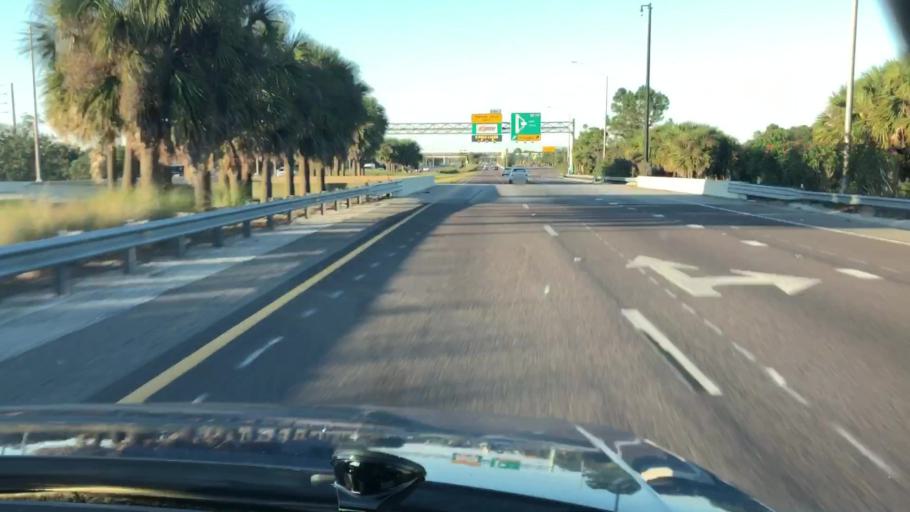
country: US
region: Florida
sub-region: Orange County
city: Paradise Heights
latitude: 28.6101
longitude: -81.5370
